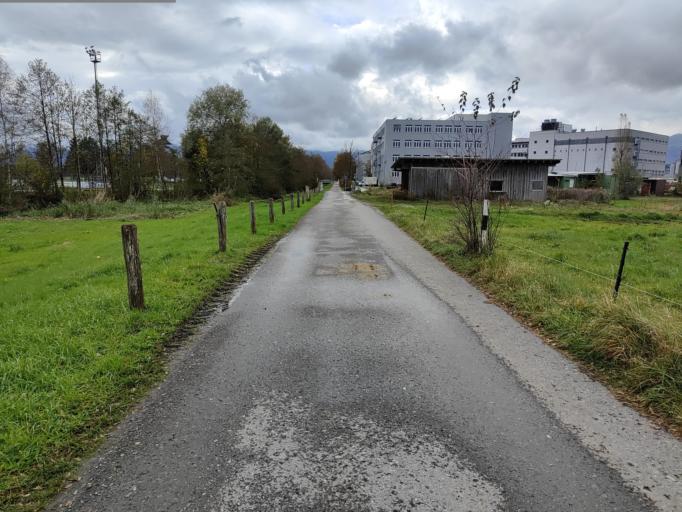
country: LI
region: Mauren
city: Mauren
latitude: 47.2069
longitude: 9.5379
